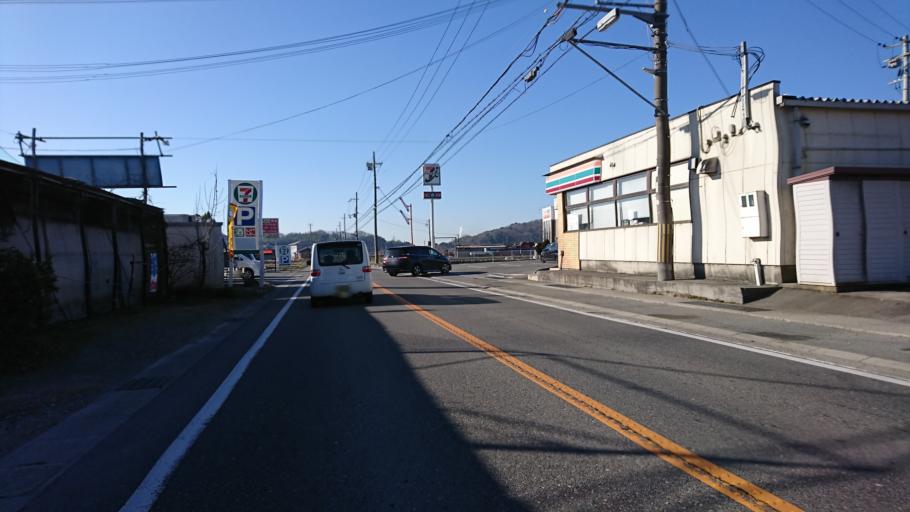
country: JP
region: Hyogo
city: Kakogawacho-honmachi
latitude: 34.8297
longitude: 134.8379
